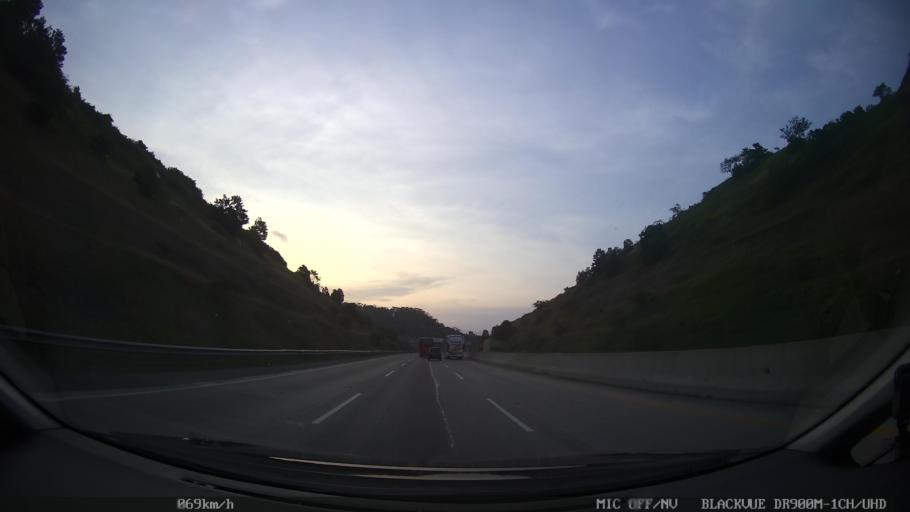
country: ID
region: Lampung
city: Penengahan
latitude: -5.8613
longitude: 105.7369
